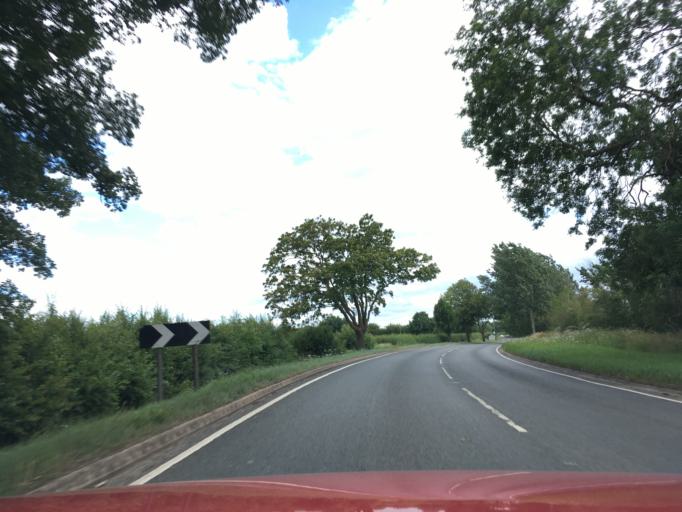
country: GB
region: England
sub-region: Warwickshire
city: Nuneaton
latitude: 52.5490
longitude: -1.4739
